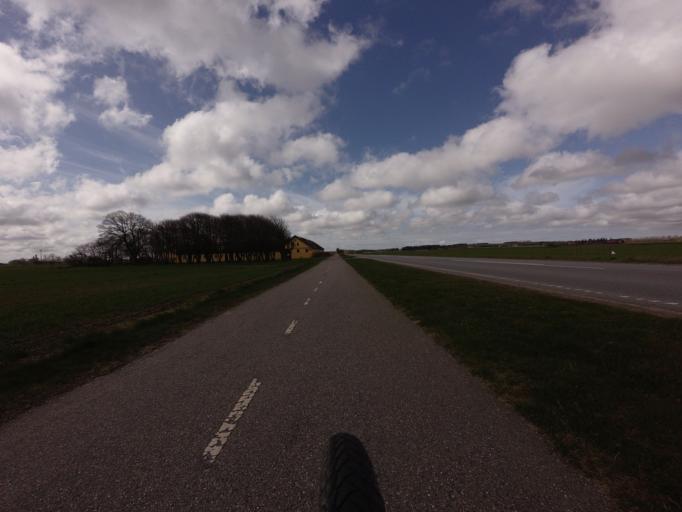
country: DK
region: North Denmark
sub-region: Hjorring Kommune
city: Vra
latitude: 57.3528
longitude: 9.9072
